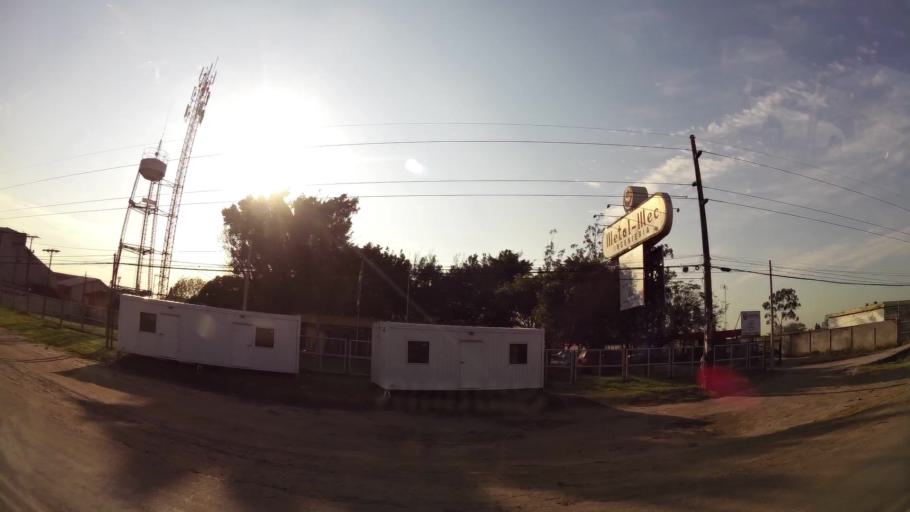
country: BO
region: Santa Cruz
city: Santa Cruz de la Sierra
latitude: -17.6986
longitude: -63.1596
